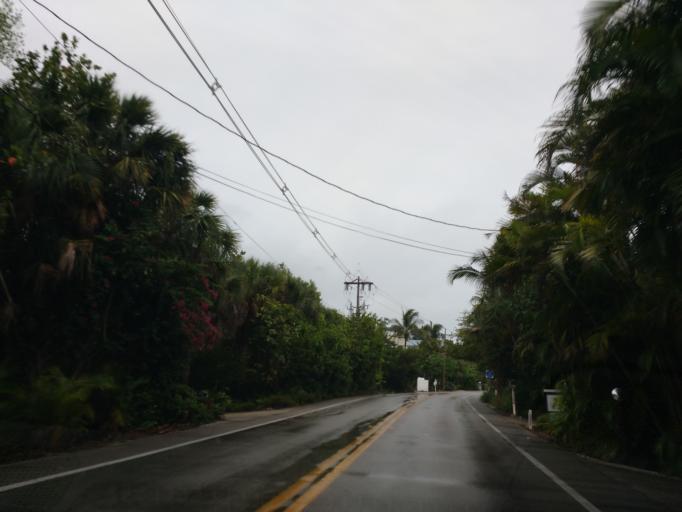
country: US
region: Florida
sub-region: Lee County
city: Saint James City
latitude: 26.4853
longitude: -82.1835
